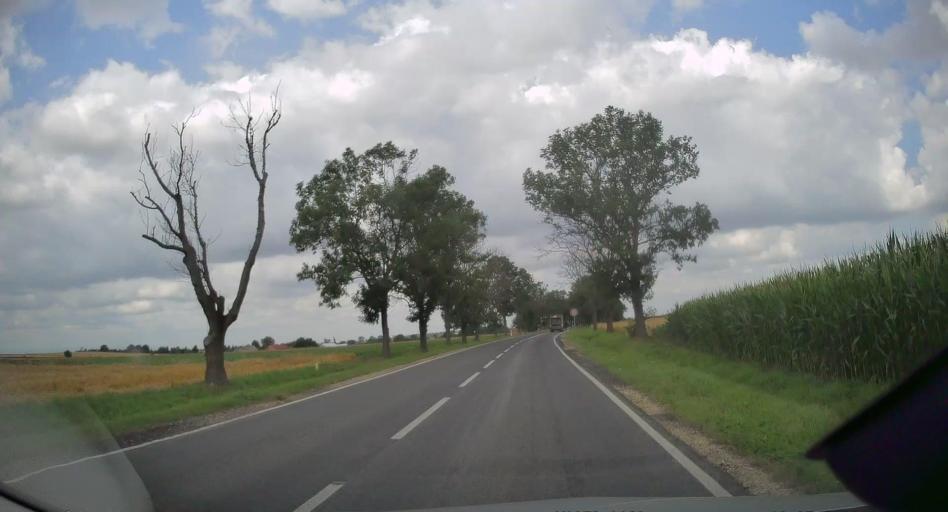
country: PL
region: Opole Voivodeship
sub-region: Powiat prudnicki
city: Glogowek
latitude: 50.3387
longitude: 17.9187
